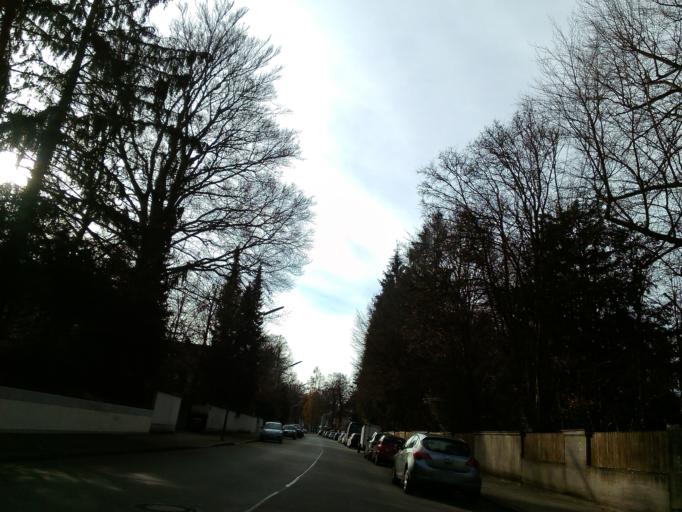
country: DE
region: Bavaria
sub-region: Upper Bavaria
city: Pullach im Isartal
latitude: 48.0887
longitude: 11.5516
